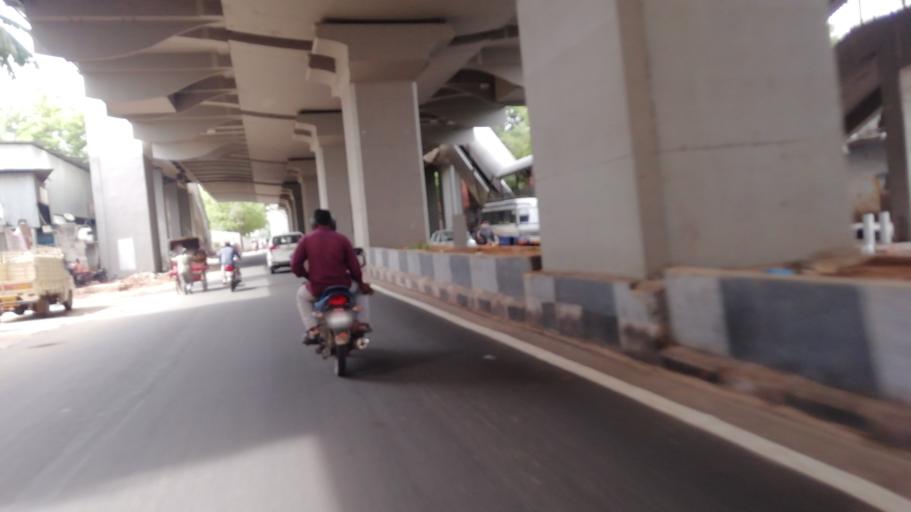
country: IN
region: Telangana
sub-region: Hyderabad
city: Malkajgiri
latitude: 17.4177
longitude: 78.4993
